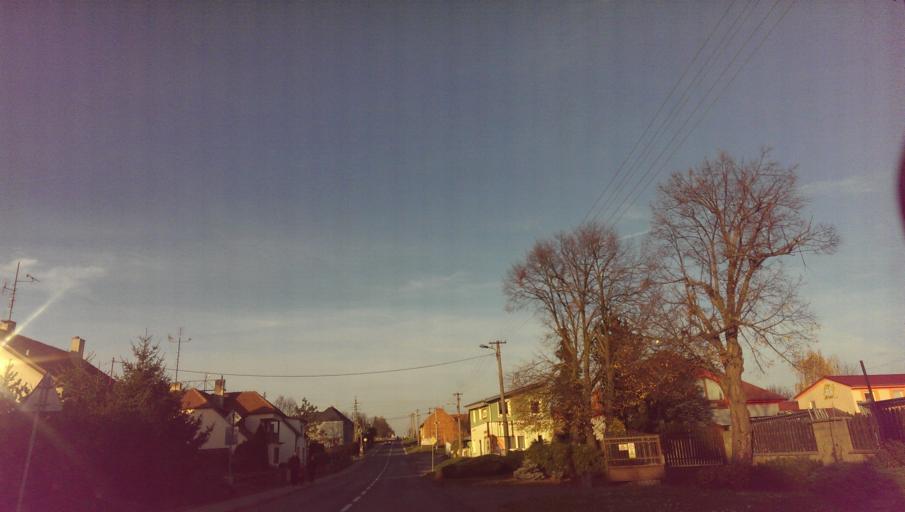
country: CZ
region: Zlin
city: Bilovice
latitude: 49.1017
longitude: 17.5550
